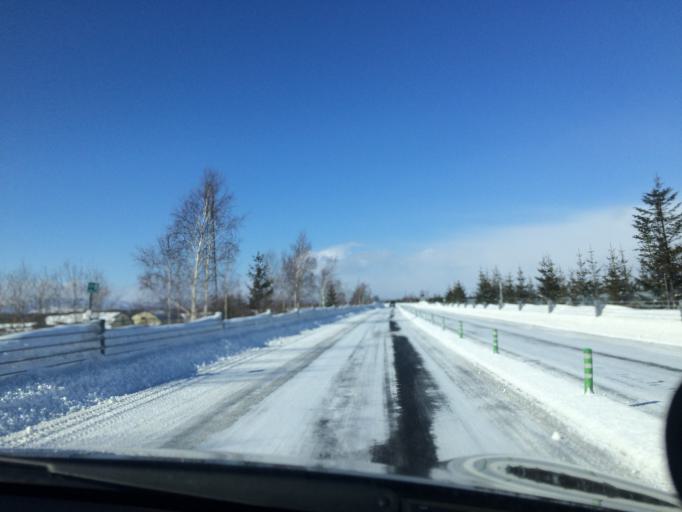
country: JP
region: Hokkaido
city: Chitose
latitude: 42.8823
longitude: 141.6392
